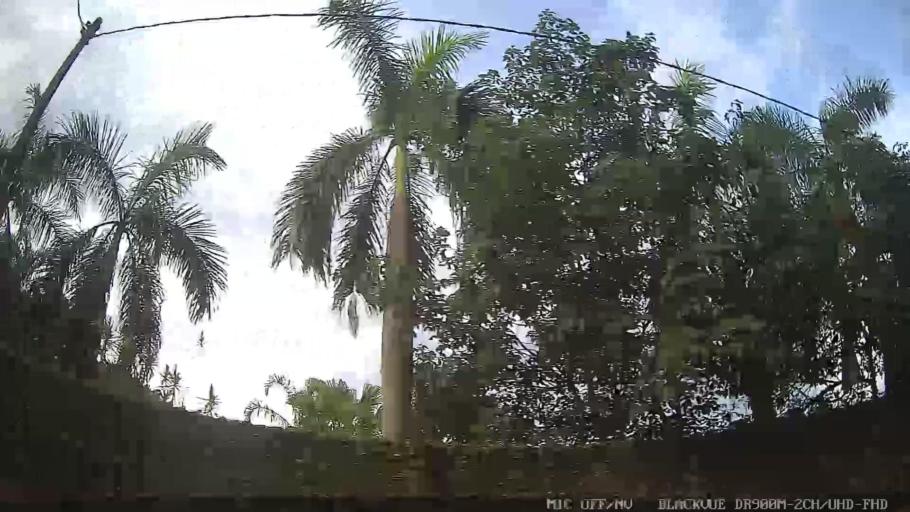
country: BR
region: Sao Paulo
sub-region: Jaguariuna
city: Jaguariuna
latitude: -22.6385
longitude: -47.0493
